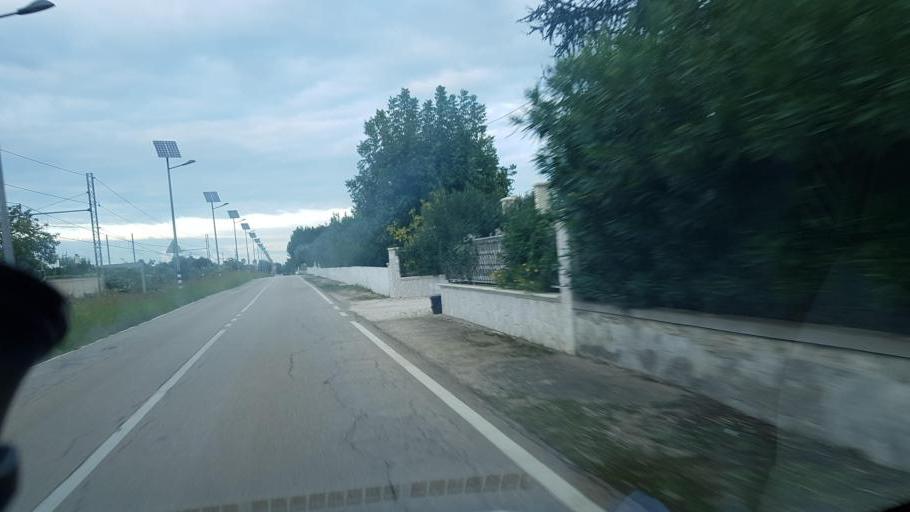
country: IT
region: Apulia
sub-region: Provincia di Brindisi
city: Latiano
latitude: 40.5407
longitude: 17.6955
